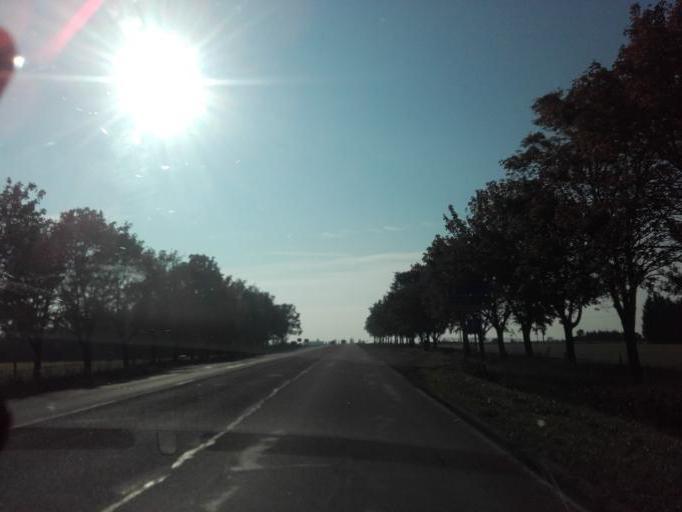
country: FR
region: Bourgogne
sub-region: Departement de Saone-et-Loire
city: Chagny
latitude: 46.8942
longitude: 4.7645
